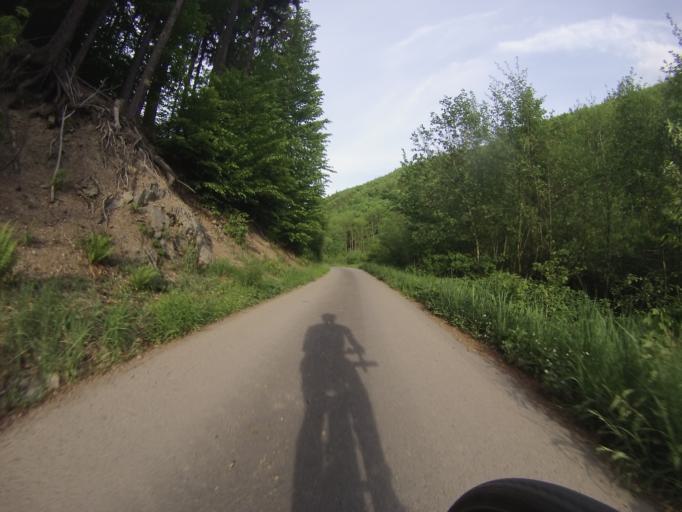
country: CZ
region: Olomoucky
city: Pteni
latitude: 49.4798
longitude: 16.9090
